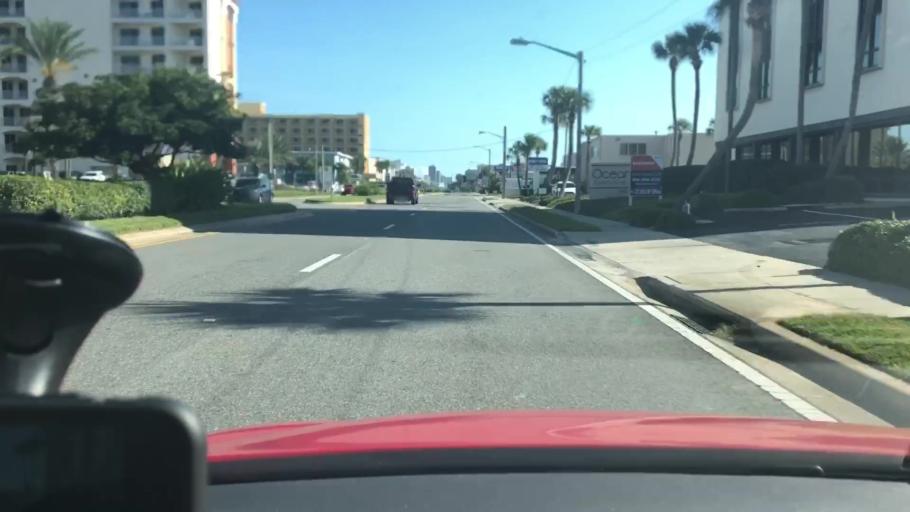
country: US
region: Florida
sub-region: Volusia County
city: Ormond Beach
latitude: 29.2887
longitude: -81.0386
